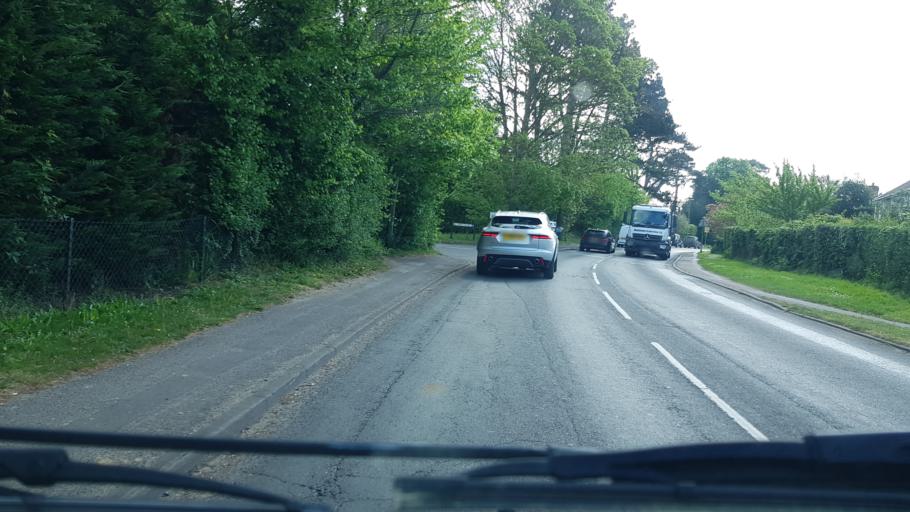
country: GB
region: England
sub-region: Surrey
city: Cobham
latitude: 51.3226
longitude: -0.3883
